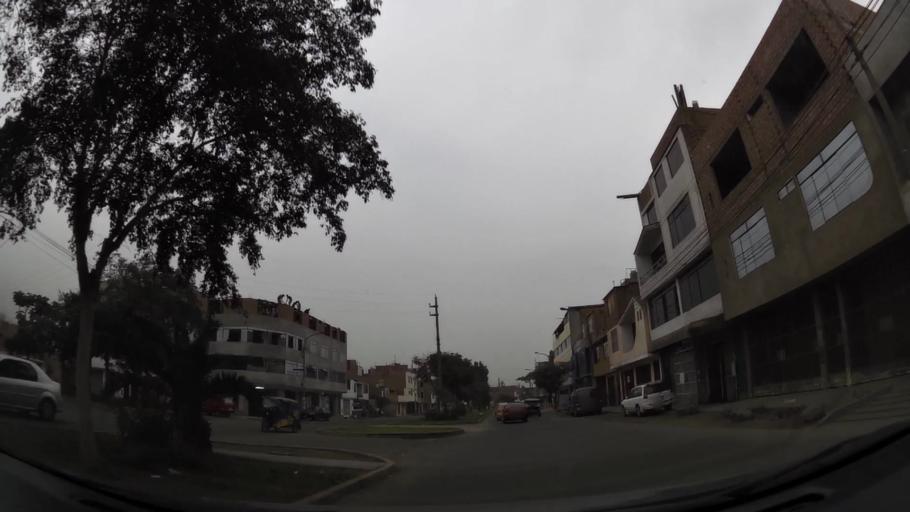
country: PE
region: Lima
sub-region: Lima
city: Urb. Santo Domingo
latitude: -11.9252
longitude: -77.0547
